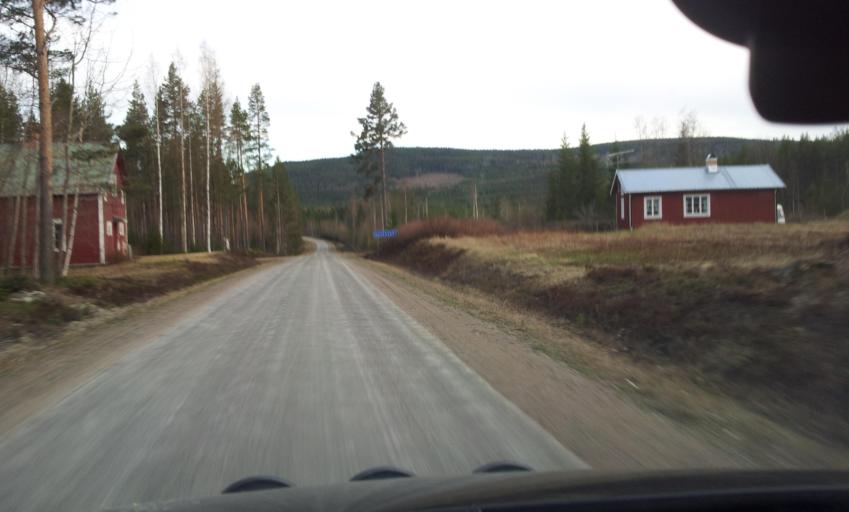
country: SE
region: Gaevleborg
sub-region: Ljusdals Kommun
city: Farila
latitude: 62.0465
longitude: 15.8236
